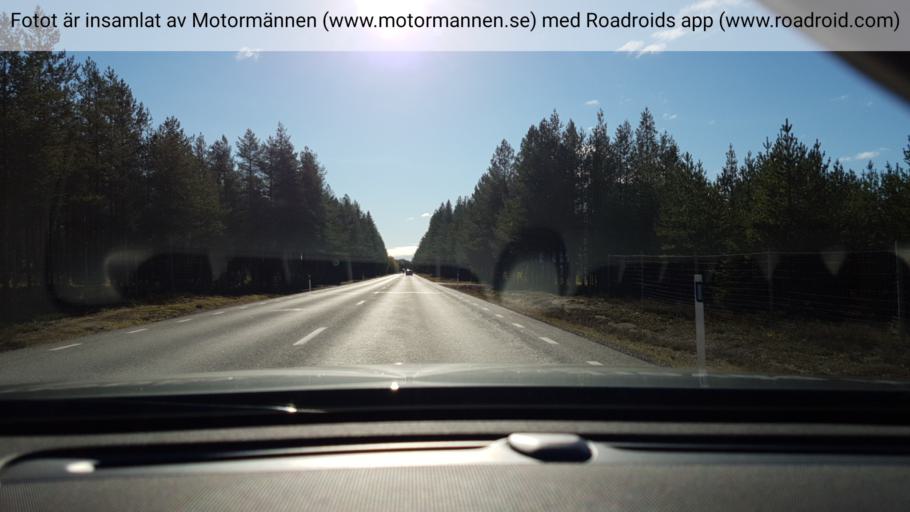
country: SE
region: Vaesterbotten
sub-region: Skelleftea Kommun
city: Burea
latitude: 64.5626
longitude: 21.2331
